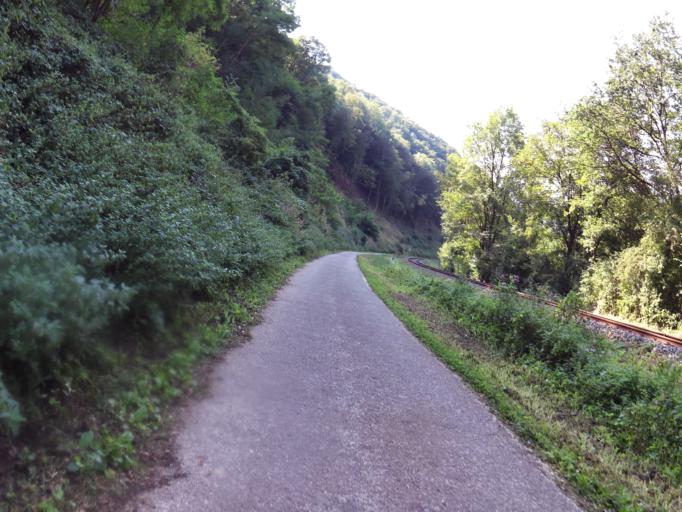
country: DE
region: Rheinland-Pfalz
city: Hosten
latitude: 49.8904
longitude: 6.6069
